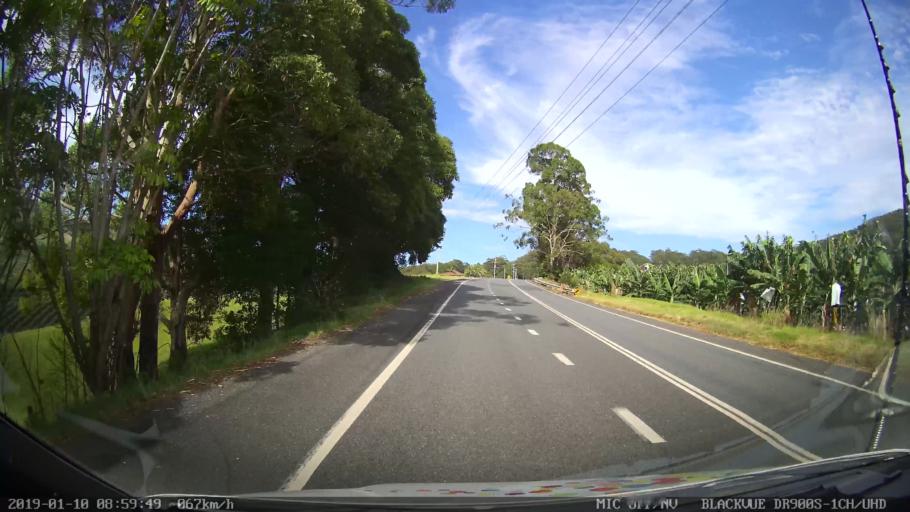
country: AU
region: New South Wales
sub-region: Coffs Harbour
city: Coffs Harbour
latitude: -30.2842
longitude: 153.0746
